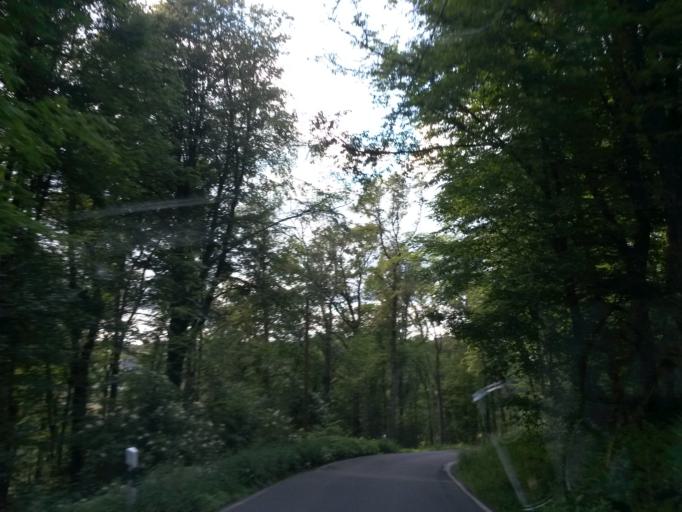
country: DE
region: North Rhine-Westphalia
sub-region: Regierungsbezirk Koln
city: Overath
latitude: 50.8802
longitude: 7.3058
